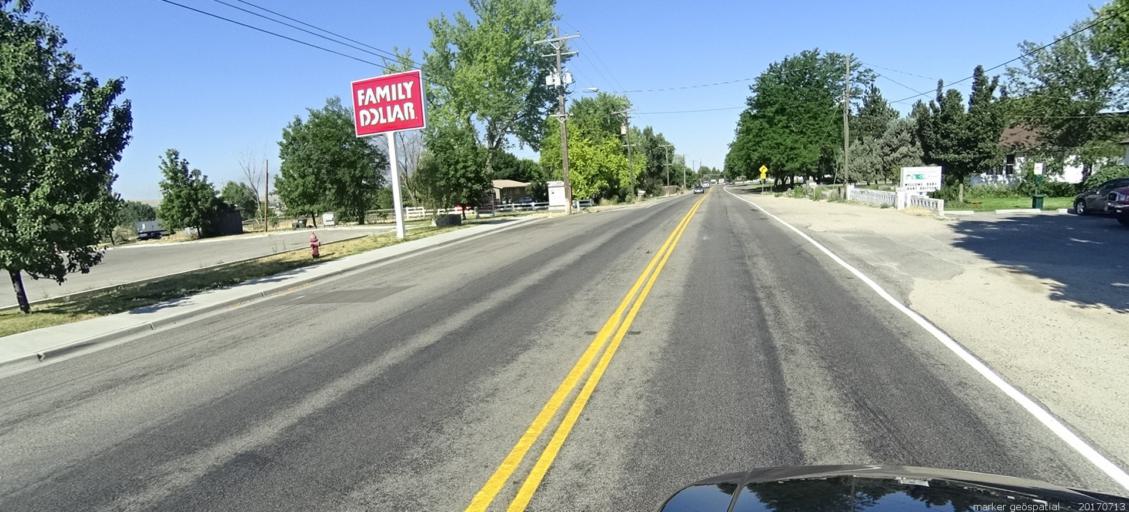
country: US
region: Idaho
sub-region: Ada County
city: Kuna
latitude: 43.4884
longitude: -116.4100
